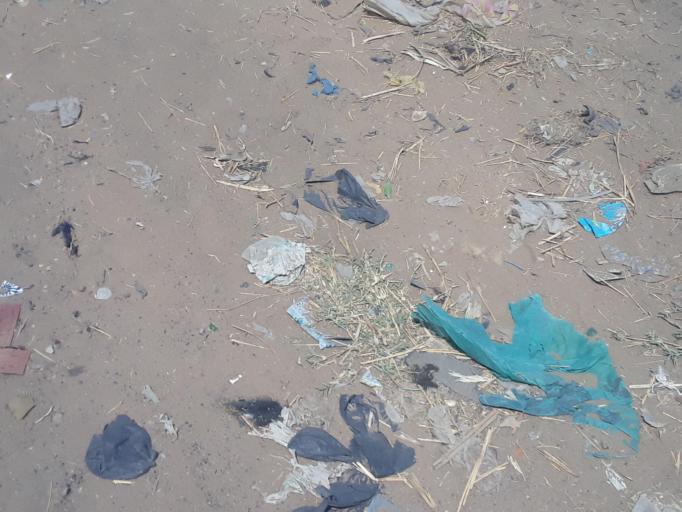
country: ZM
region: Lusaka
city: Lusaka
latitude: -15.3673
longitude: 28.2903
